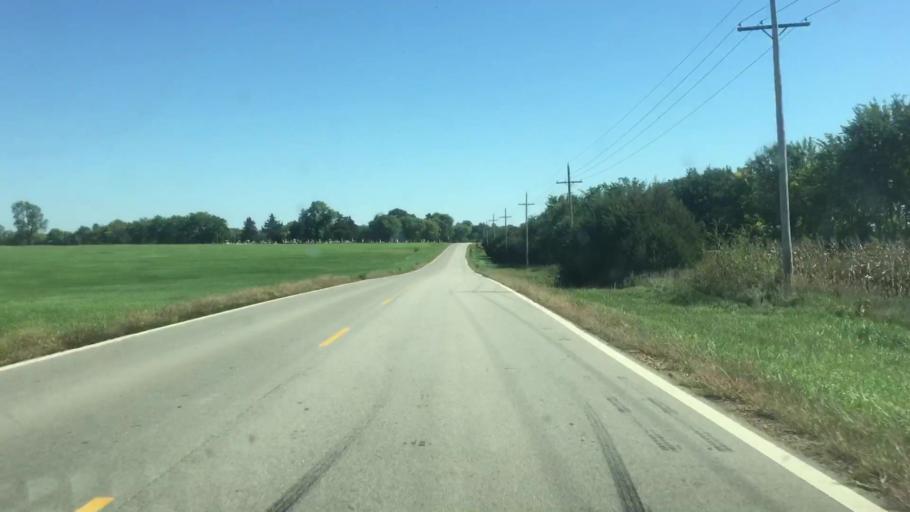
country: US
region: Kansas
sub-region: Jackson County
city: Holton
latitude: 39.6109
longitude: -95.7272
